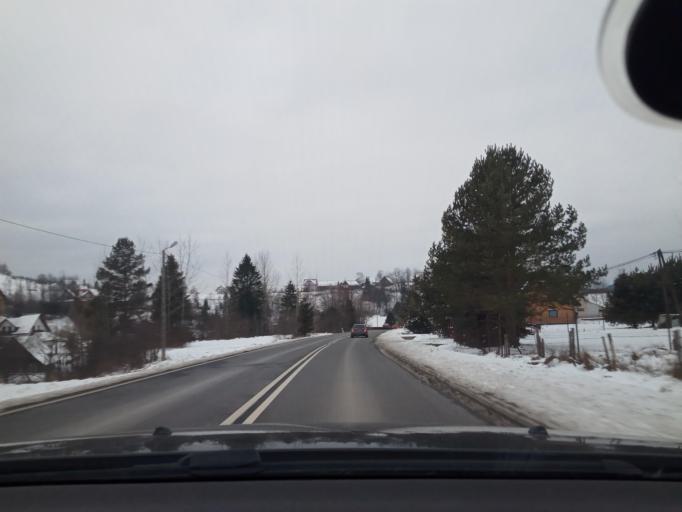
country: PL
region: Lesser Poland Voivodeship
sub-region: Powiat limanowski
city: Lubomierz
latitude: 49.6083
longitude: 20.1978
